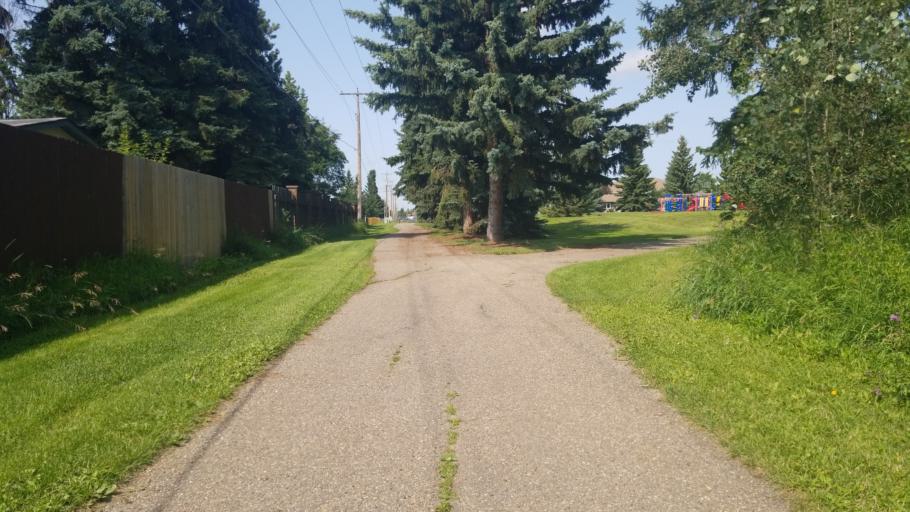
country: CA
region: Saskatchewan
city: Lloydminster
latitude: 53.2718
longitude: -110.0176
